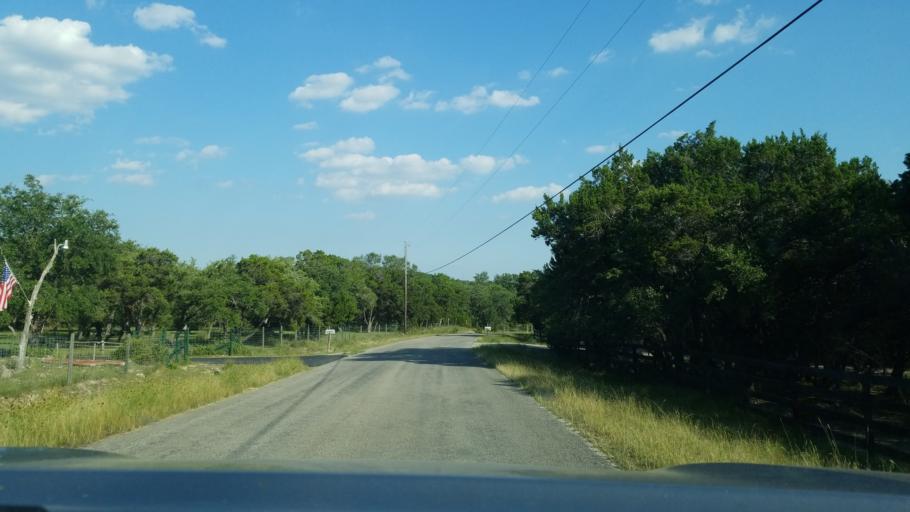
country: US
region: Texas
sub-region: Comal County
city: Bulverde
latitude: 29.7917
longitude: -98.4283
